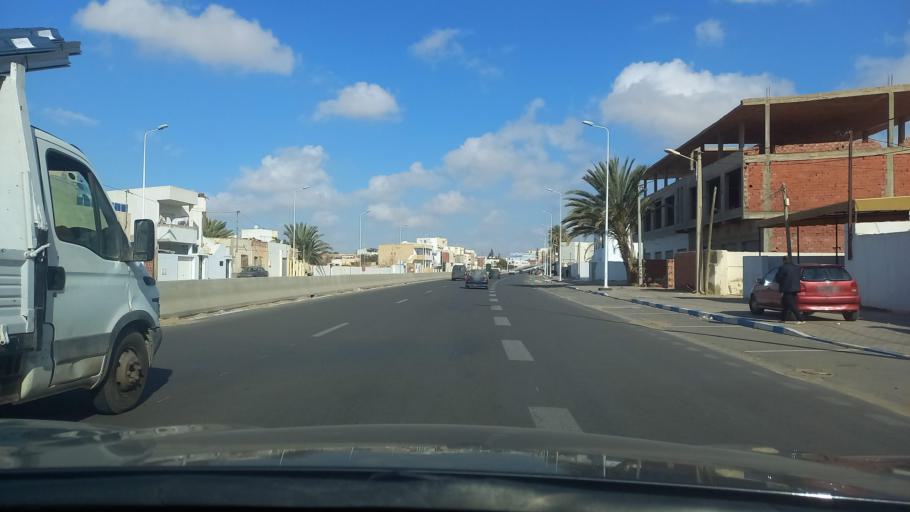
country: TN
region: Safaqis
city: Sfax
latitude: 34.7408
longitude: 10.7239
